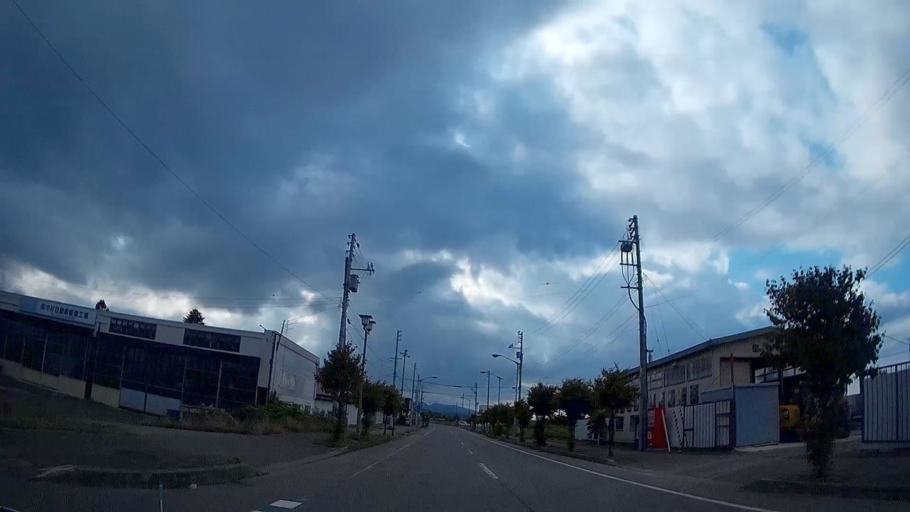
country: JP
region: Hokkaido
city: Nanae
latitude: 42.1096
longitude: 140.5679
